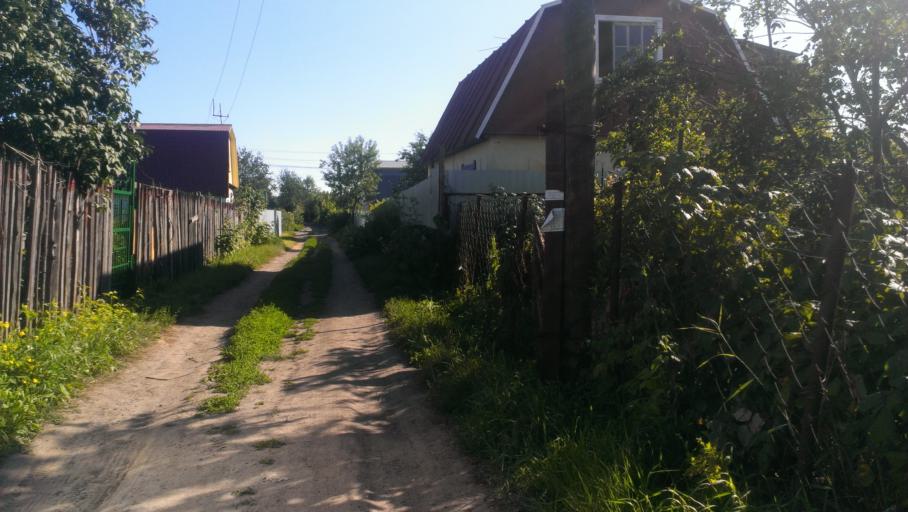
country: RU
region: Altai Krai
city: Novosilikatnyy
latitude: 53.3243
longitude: 83.6696
